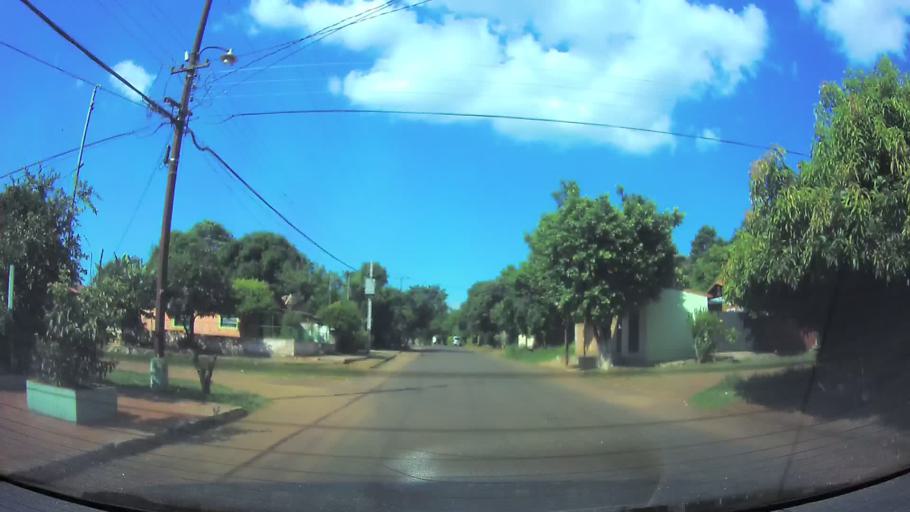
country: PY
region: Central
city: Itaugua
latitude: -25.3881
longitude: -57.3481
